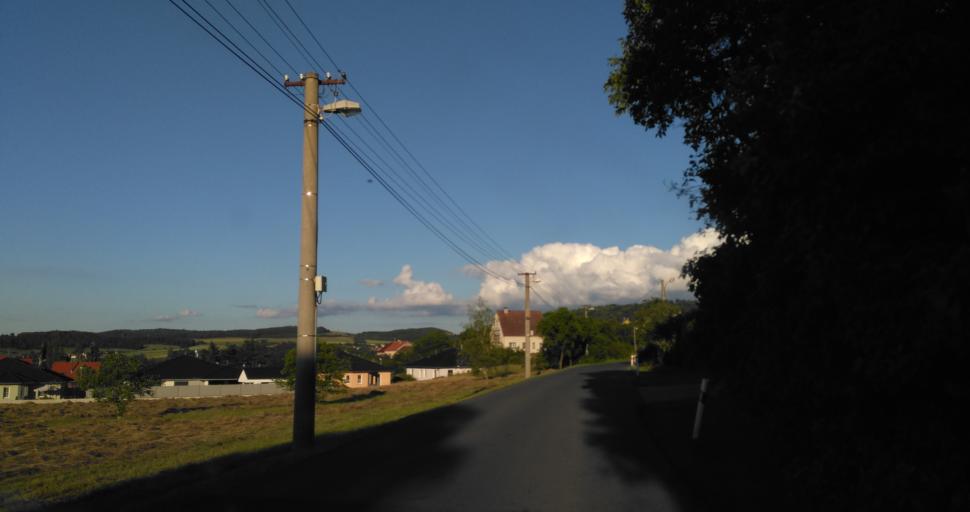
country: CZ
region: Central Bohemia
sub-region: Okres Beroun
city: Kraluv Dvur
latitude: 49.9256
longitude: 14.0330
